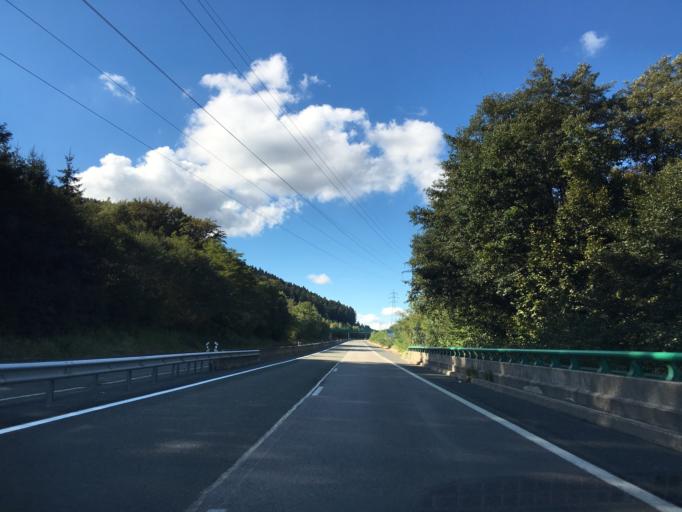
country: FR
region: Lorraine
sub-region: Departement des Vosges
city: Etival-Clairefontaine
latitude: 48.3936
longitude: 6.8556
